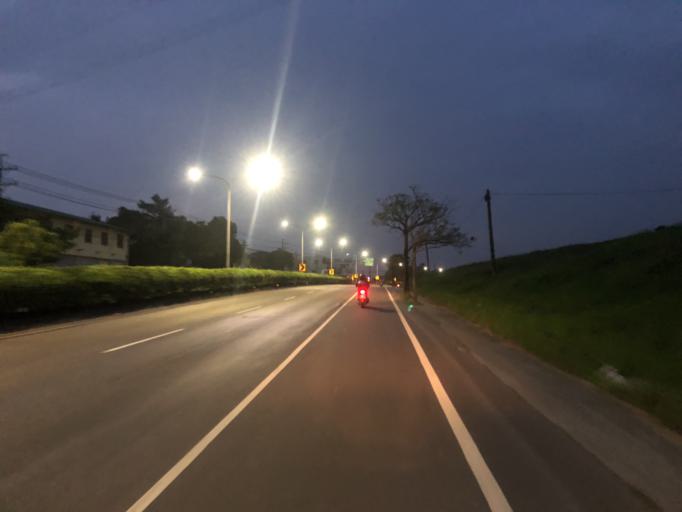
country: TW
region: Taiwan
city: Yujing
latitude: 23.1693
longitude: 120.3392
